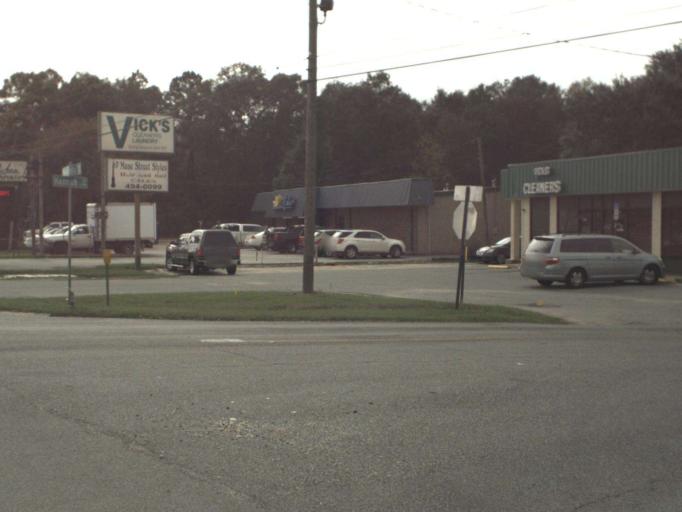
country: US
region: Florida
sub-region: Escambia County
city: Ensley
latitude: 30.5235
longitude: -87.2741
